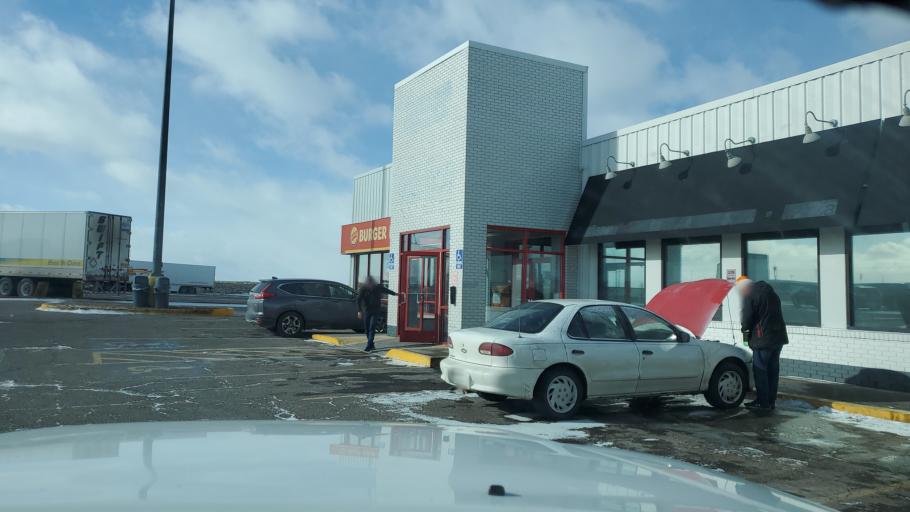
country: US
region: Wyoming
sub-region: Uinta County
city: Mountain View
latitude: 41.3142
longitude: -110.5094
